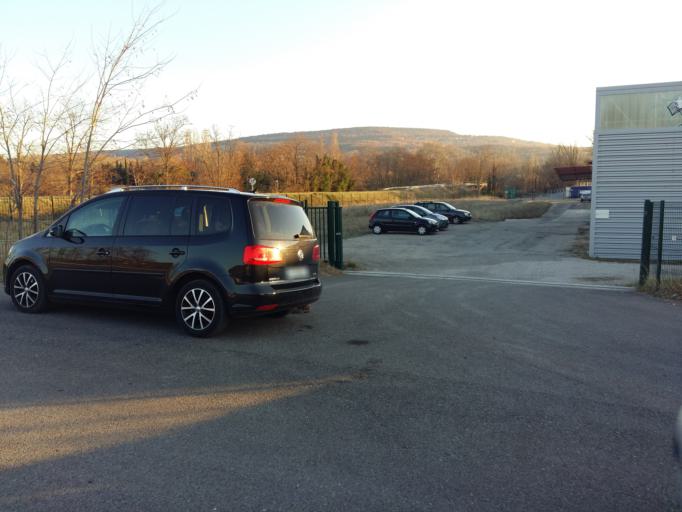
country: FR
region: Rhone-Alpes
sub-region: Departement de la Drome
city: La Garde-Adhemar
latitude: 44.4172
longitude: 4.8065
